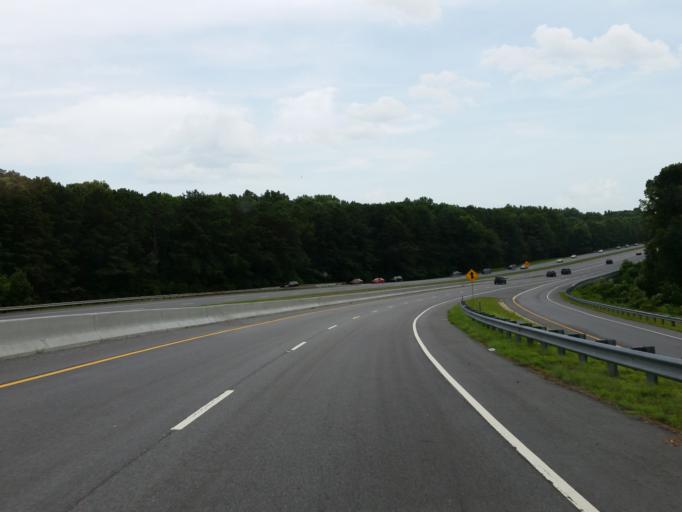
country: US
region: Georgia
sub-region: Cobb County
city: Marietta
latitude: 33.9595
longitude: -84.4968
